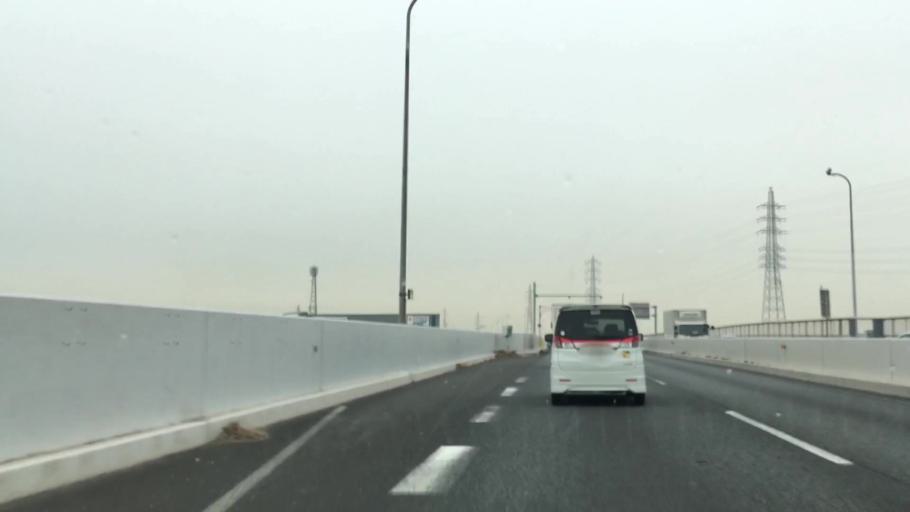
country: JP
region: Aichi
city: Chiryu
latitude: 35.0041
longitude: 137.0274
